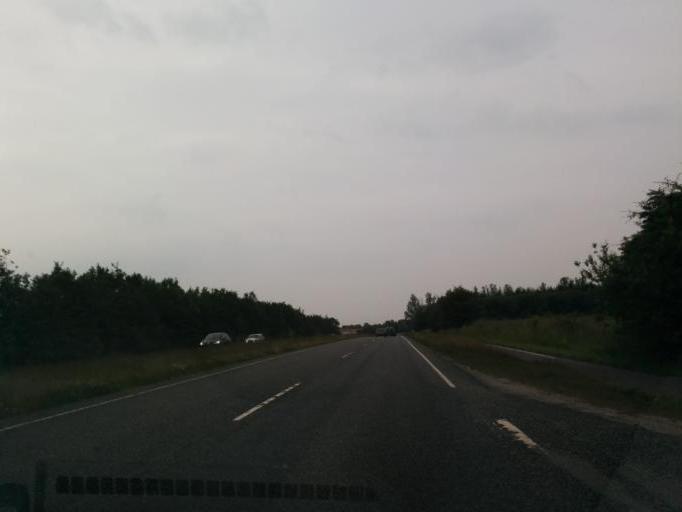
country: DK
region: Central Jutland
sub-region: Arhus Kommune
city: Hjortshoj
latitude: 56.2382
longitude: 10.2980
